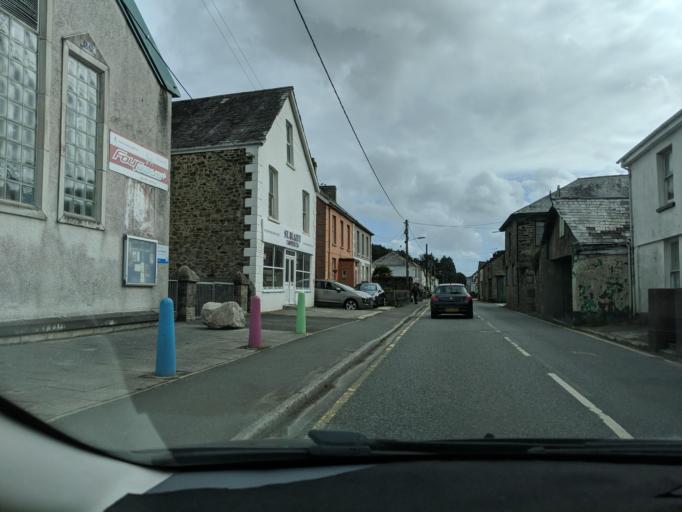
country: GB
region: England
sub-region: Cornwall
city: Par
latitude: 50.3598
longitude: -4.7145
